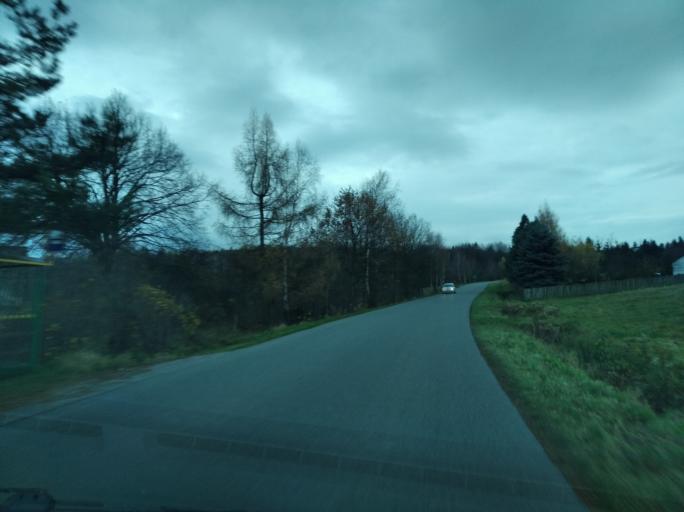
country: PL
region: Subcarpathian Voivodeship
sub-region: Powiat ropczycko-sedziszowski
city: Zagorzyce
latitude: 49.9701
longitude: 21.7008
